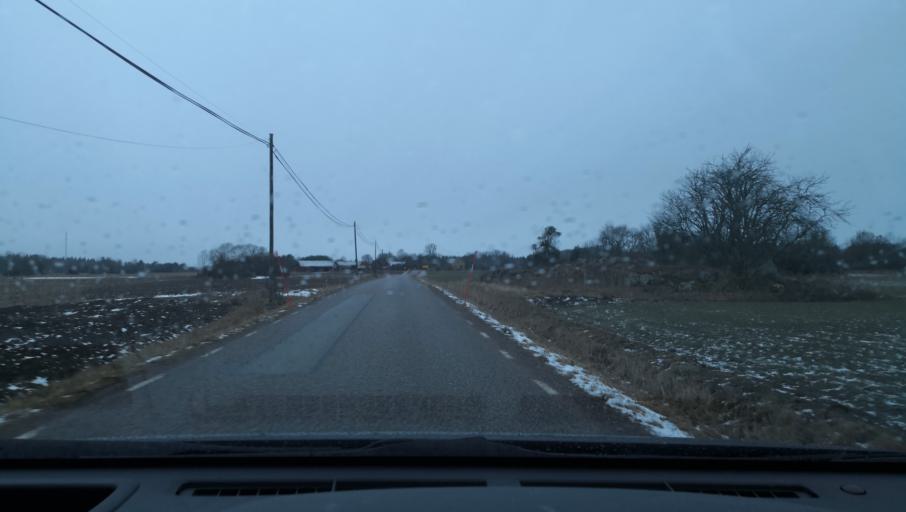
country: SE
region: Soedermanland
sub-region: Strangnas Kommun
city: Strangnas
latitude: 59.4505
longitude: 16.8690
